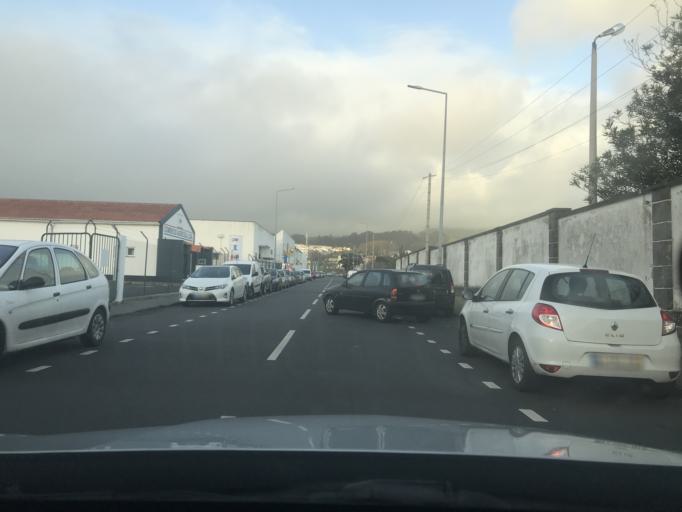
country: PT
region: Azores
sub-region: Angra do Heroismo
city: Angra do Heroismo
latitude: 38.6542
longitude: -27.2111
